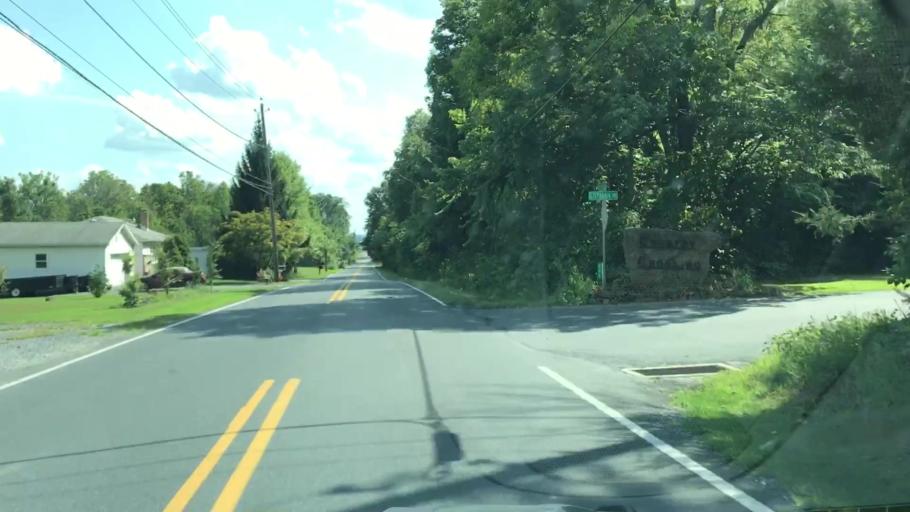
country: US
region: Pennsylvania
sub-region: Dauphin County
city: Middletown
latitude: 40.1891
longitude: -76.6932
